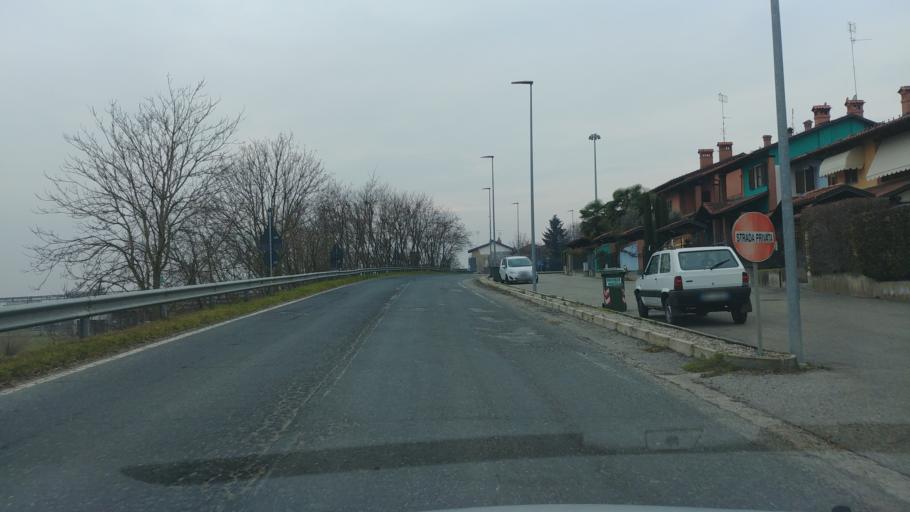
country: IT
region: Piedmont
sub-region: Provincia di Cuneo
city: Fossano
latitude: 44.5424
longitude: 7.7240
